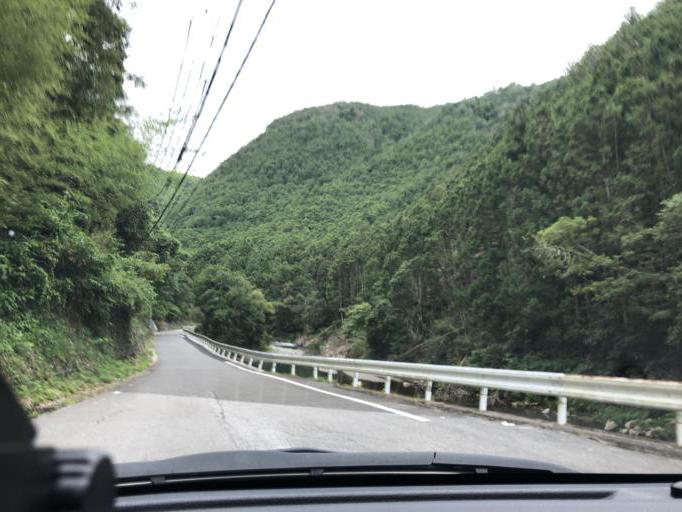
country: JP
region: Kochi
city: Kochi-shi
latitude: 33.6288
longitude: 133.5077
